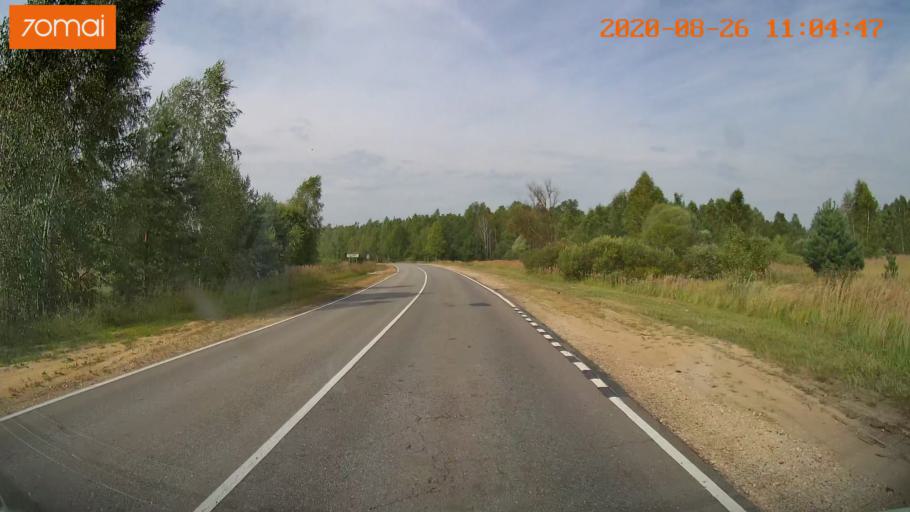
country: RU
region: Rjazan
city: Izhevskoye
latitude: 54.5294
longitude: 41.1885
